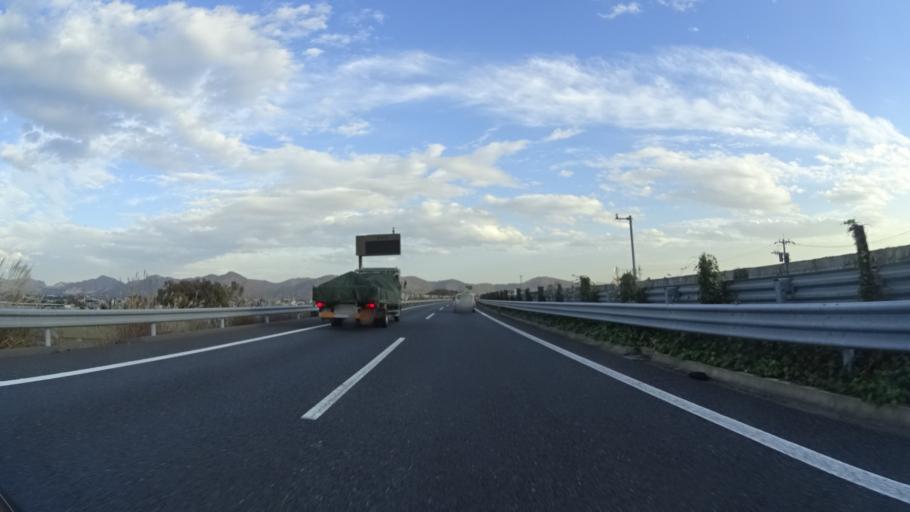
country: JP
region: Tochigi
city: Tanuma
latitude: 36.3632
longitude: 139.5640
